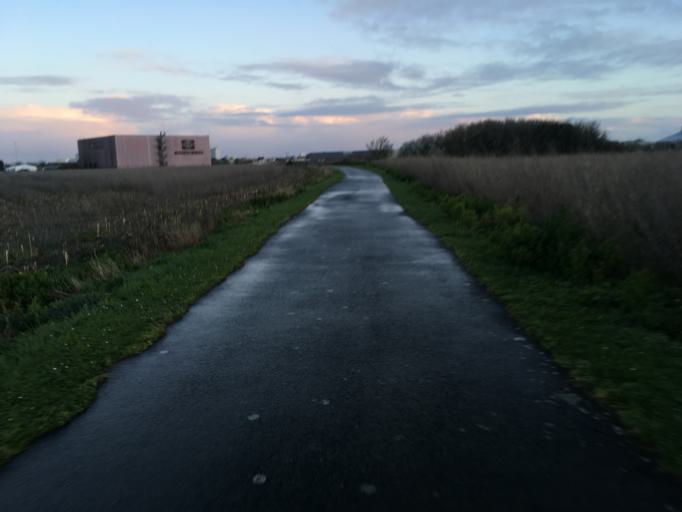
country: FR
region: Poitou-Charentes
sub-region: Departement de la Charente-Maritime
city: Nieul-sur-Mer
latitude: 46.1767
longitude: -1.2100
